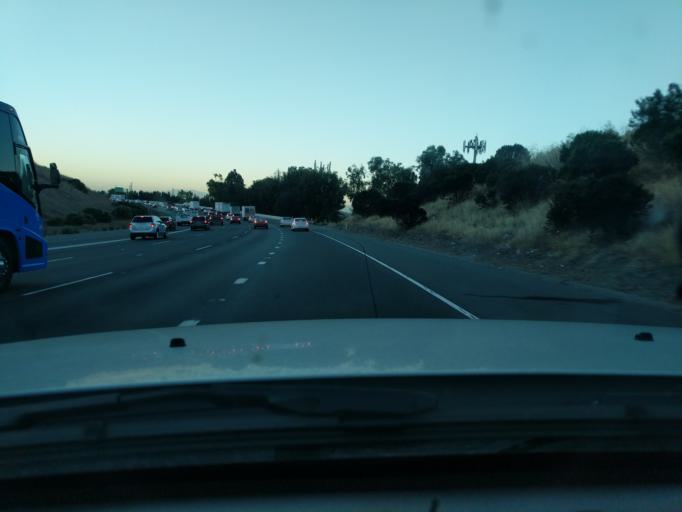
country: US
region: California
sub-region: Alameda County
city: Fremont
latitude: 37.5257
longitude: -121.9471
